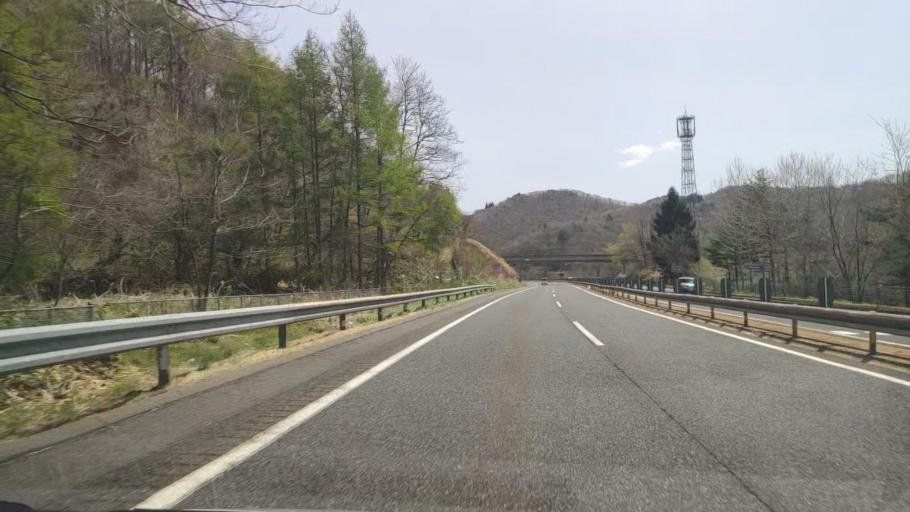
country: JP
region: Iwate
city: Ichinohe
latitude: 40.2197
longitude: 141.2410
